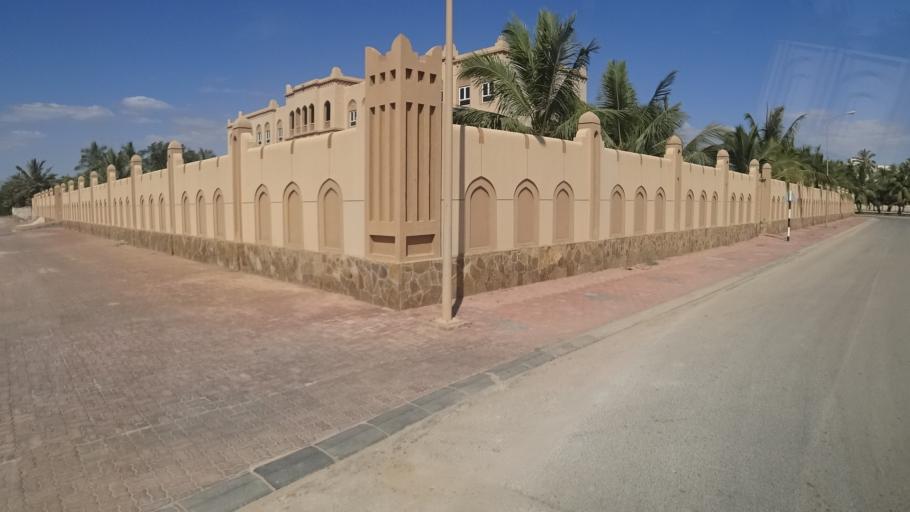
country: OM
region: Zufar
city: Salalah
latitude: 17.0017
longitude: 54.0640
